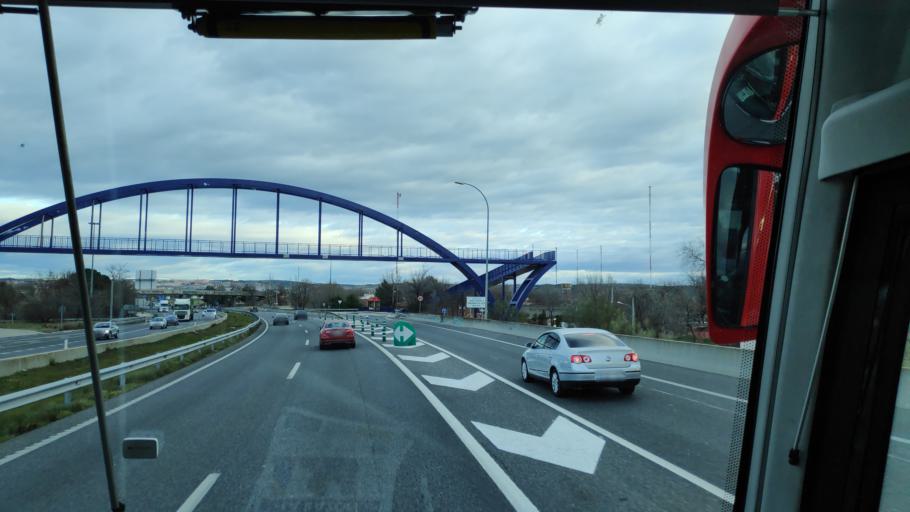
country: ES
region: Madrid
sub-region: Provincia de Madrid
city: Vaciamadrid
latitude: 40.3181
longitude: -3.5129
